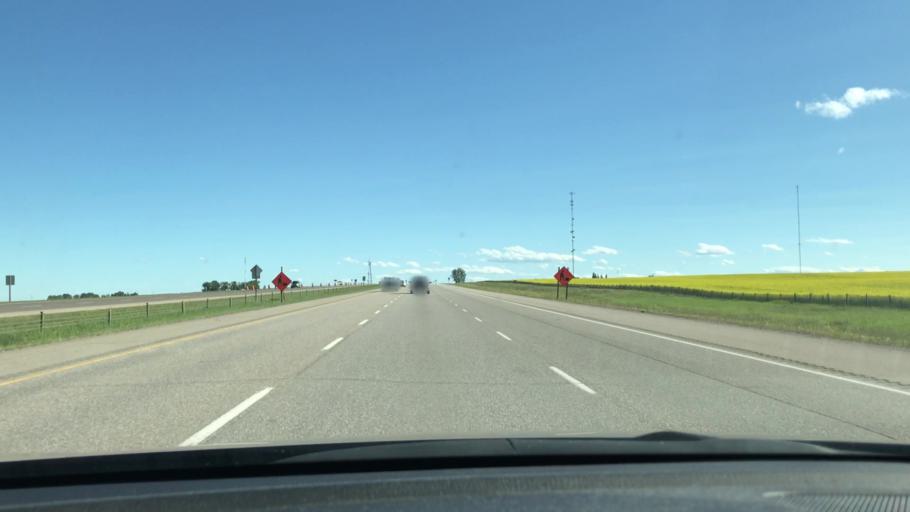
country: CA
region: Alberta
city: Crossfield
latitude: 51.4287
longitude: -114.0021
